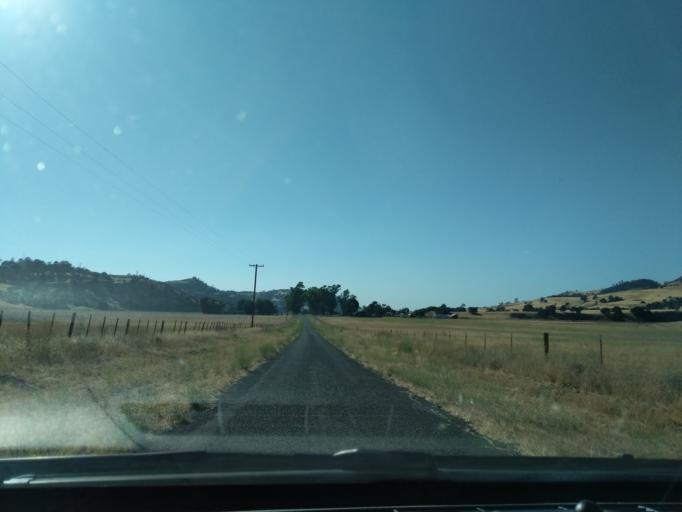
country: US
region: California
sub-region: Fresno County
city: Coalinga
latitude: 36.1081
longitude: -120.7136
